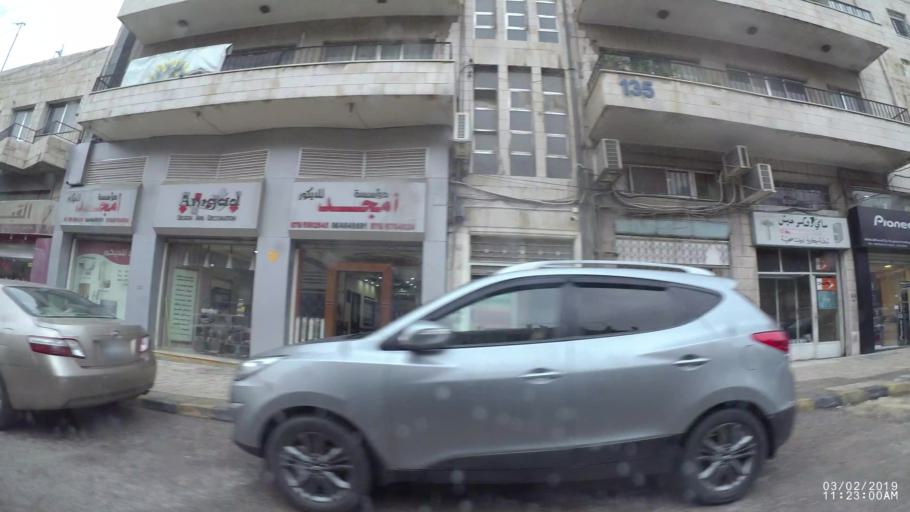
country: JO
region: Amman
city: Amman
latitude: 31.9529
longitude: 35.9243
